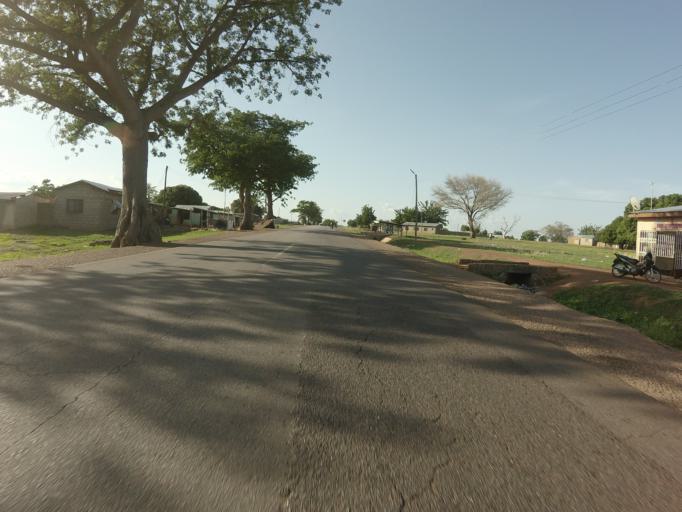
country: GH
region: Upper East
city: Navrongo
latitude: 10.9168
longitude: -1.0897
